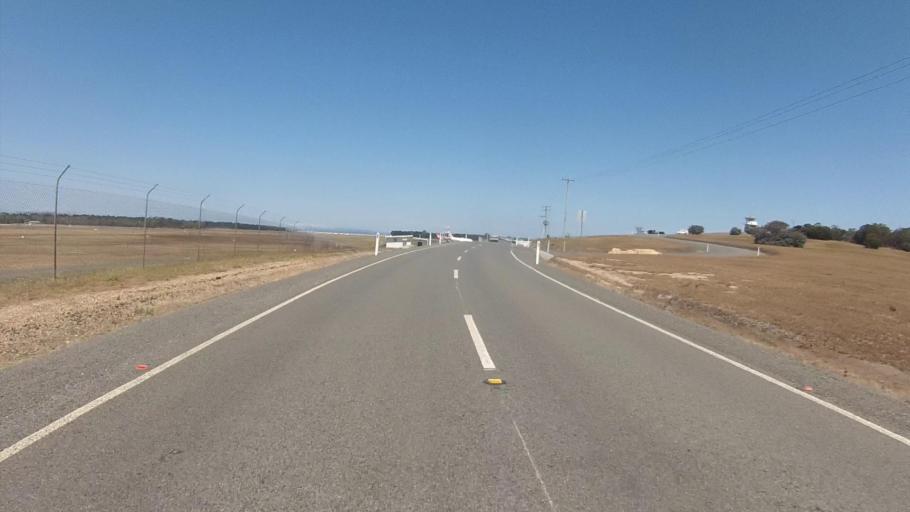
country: AU
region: Tasmania
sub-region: Clarence
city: Seven Mile Beach
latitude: -42.8319
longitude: 147.5008
